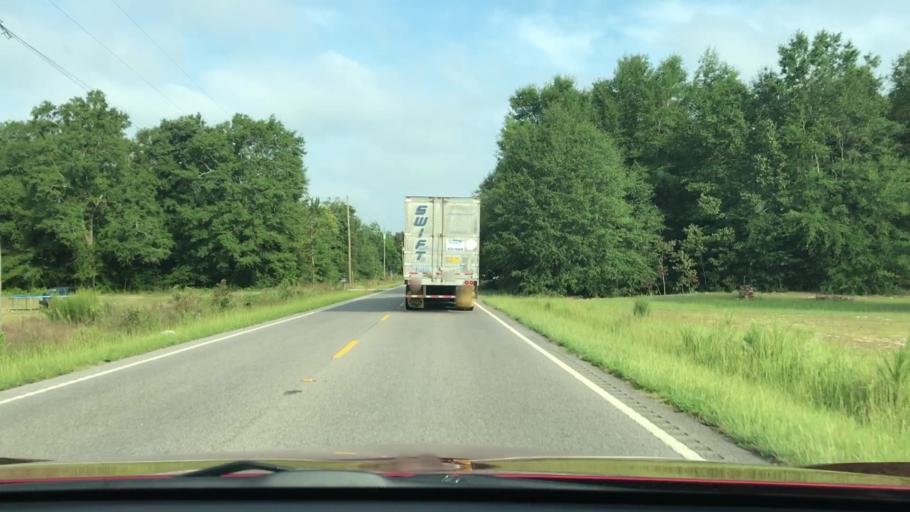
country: US
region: South Carolina
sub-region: Barnwell County
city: Williston
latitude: 33.6316
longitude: -81.3088
